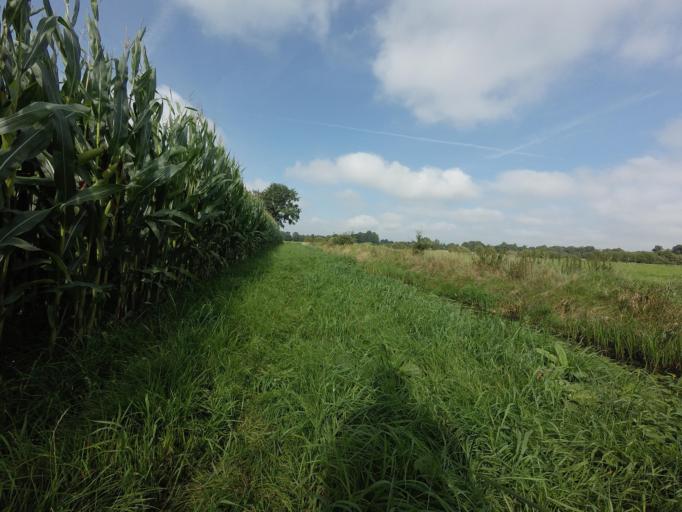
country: NL
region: Drenthe
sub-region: Gemeente Tynaarlo
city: Vries
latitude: 53.1121
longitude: 6.5495
